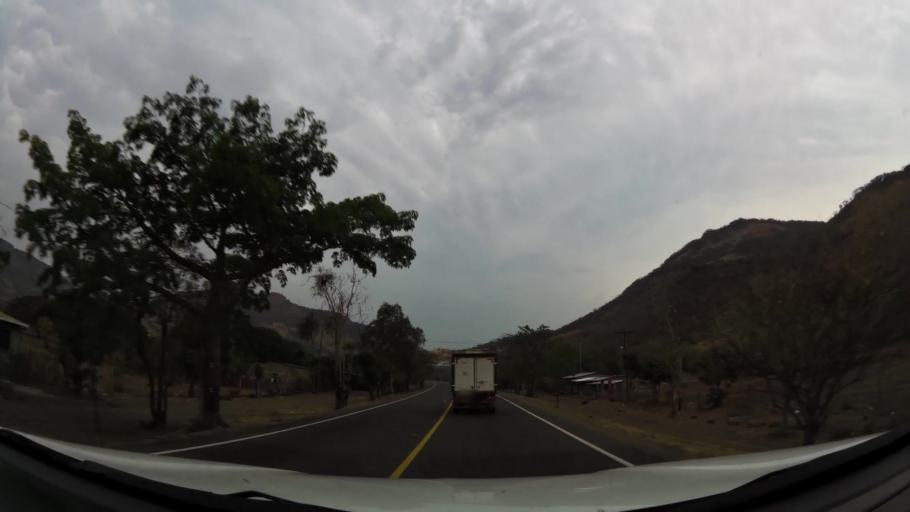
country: NI
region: Leon
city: Santa Rosa del Penon
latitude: 12.9350
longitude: -86.2014
